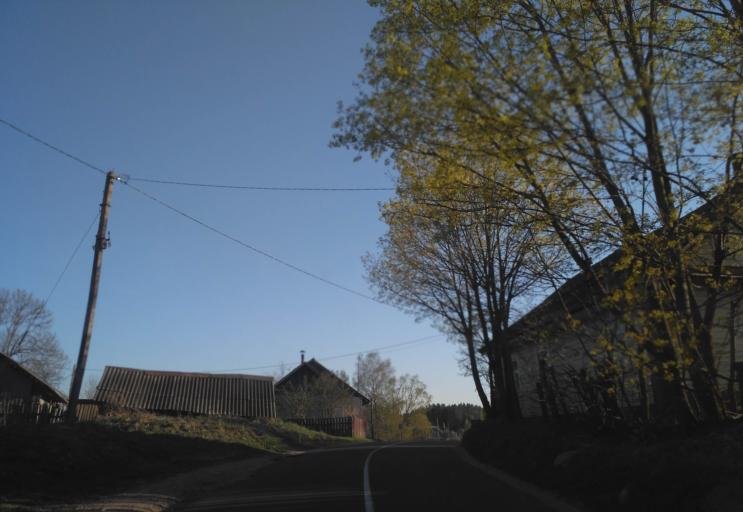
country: BY
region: Minsk
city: Radashkovichy
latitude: 54.1340
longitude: 27.2040
